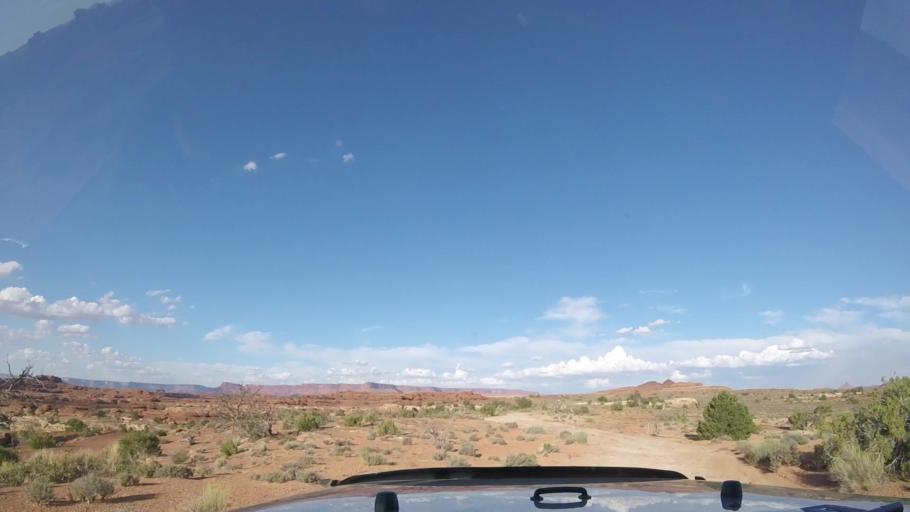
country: US
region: Utah
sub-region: Grand County
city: Moab
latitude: 38.2158
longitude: -109.7994
